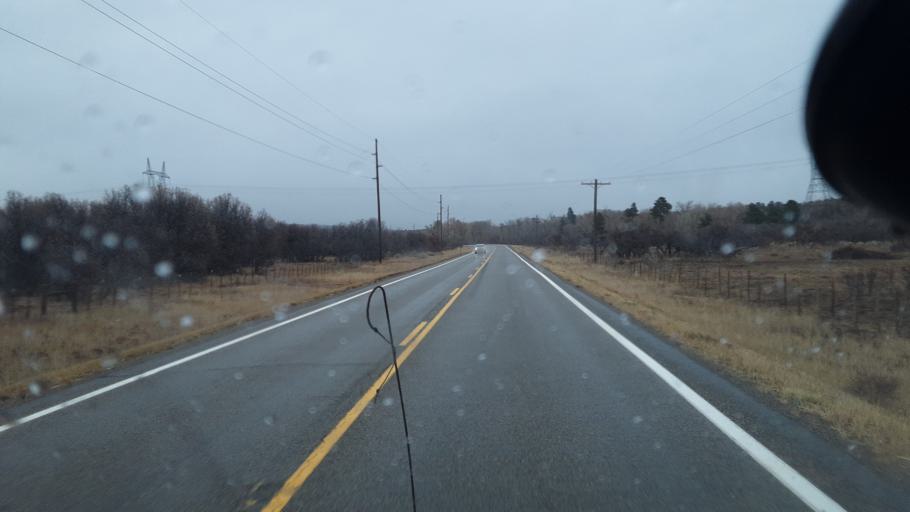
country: US
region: Colorado
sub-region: La Plata County
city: Durango
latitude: 37.2409
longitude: -108.0392
